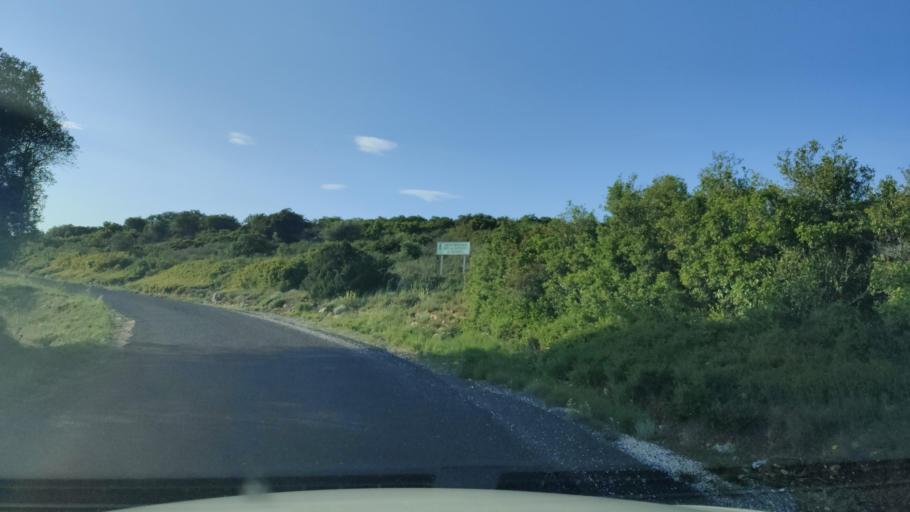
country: FR
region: Languedoc-Roussillon
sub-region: Departement des Pyrenees-Orientales
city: Estagel
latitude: 42.7878
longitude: 2.7442
